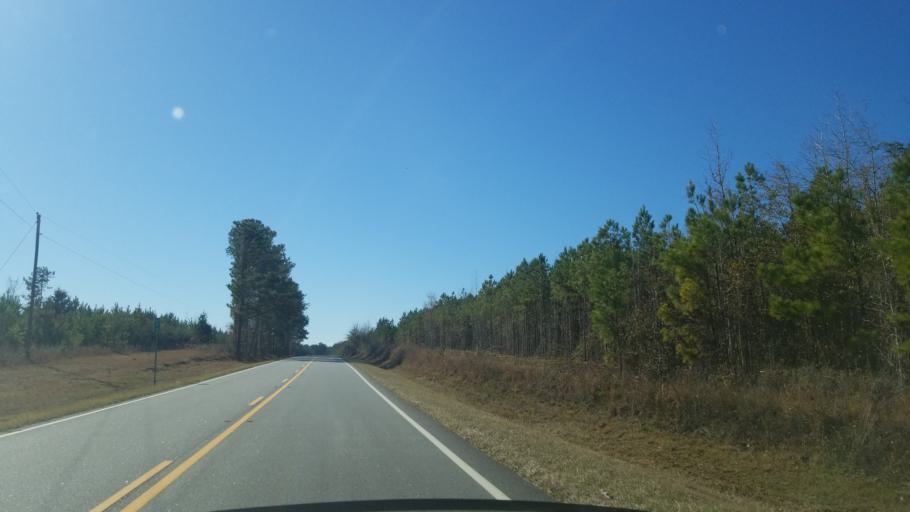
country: US
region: Georgia
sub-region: Talbot County
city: Sardis
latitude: 32.6382
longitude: -84.7168
